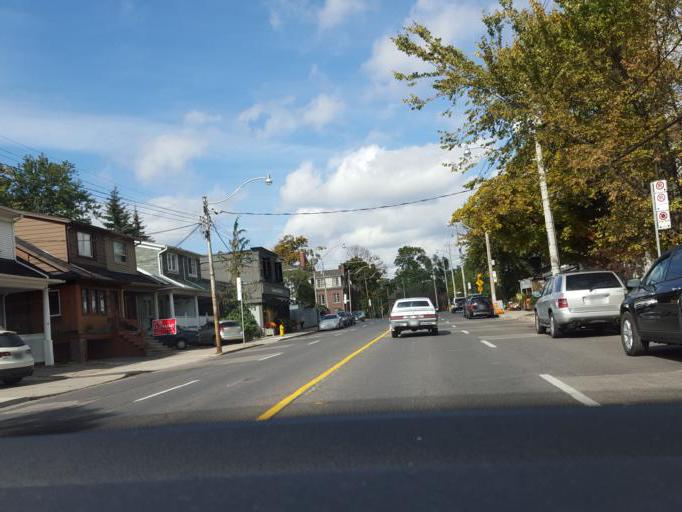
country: CA
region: Ontario
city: Toronto
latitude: 43.7151
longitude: -79.3927
